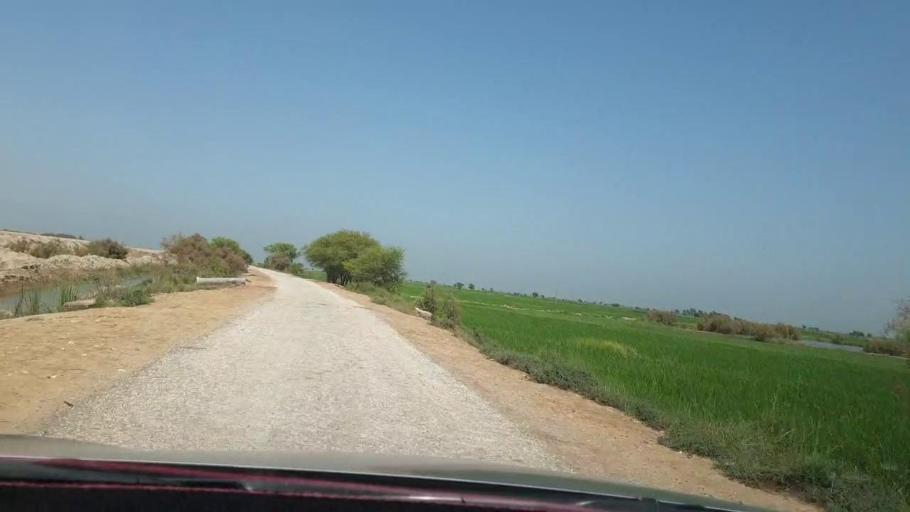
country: PK
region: Sindh
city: Warah
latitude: 27.5518
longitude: 67.7384
